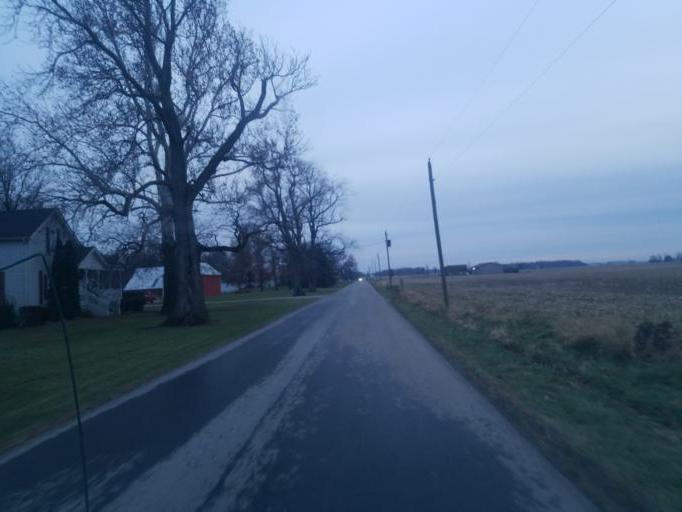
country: US
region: Indiana
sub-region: Adams County
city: Decatur
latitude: 40.7825
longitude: -85.0147
